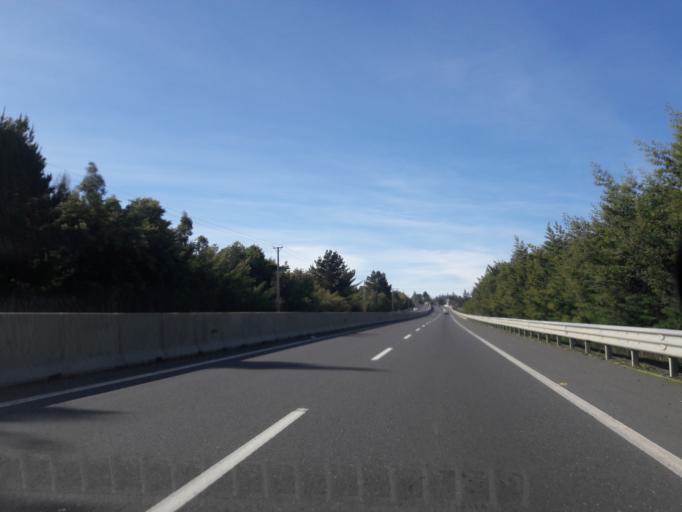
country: CL
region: Biobio
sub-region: Provincia de Biobio
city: Yumbel
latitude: -36.9744
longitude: -72.6623
